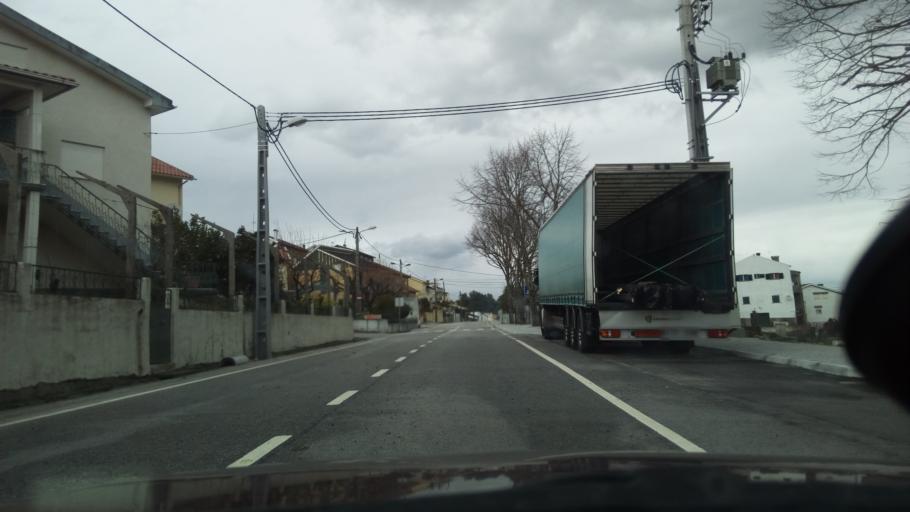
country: PT
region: Guarda
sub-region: Fornos de Algodres
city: Fornos de Algodres
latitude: 40.5234
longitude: -7.5804
